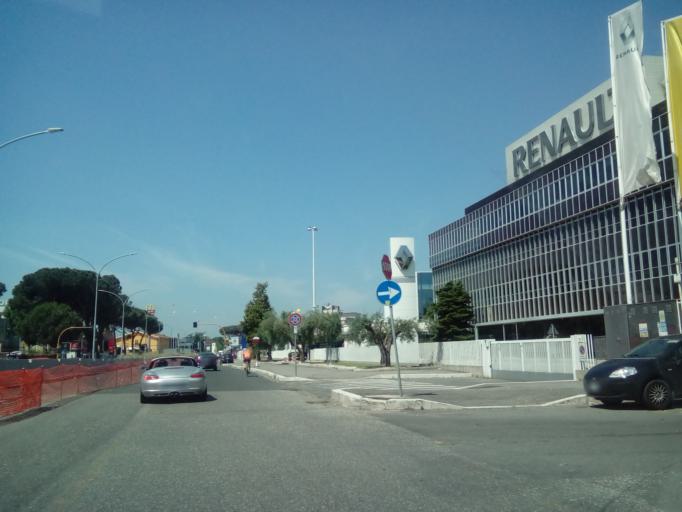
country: IT
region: Latium
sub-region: Citta metropolitana di Roma Capitale
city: Colle Verde
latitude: 41.9331
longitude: 12.5985
